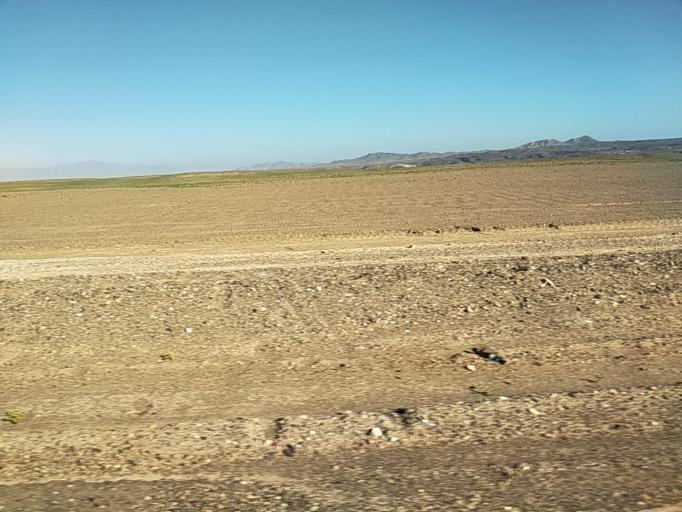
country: CL
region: Atacama
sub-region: Provincia de Copiapo
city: Copiapo
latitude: -27.3286
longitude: -70.7665
